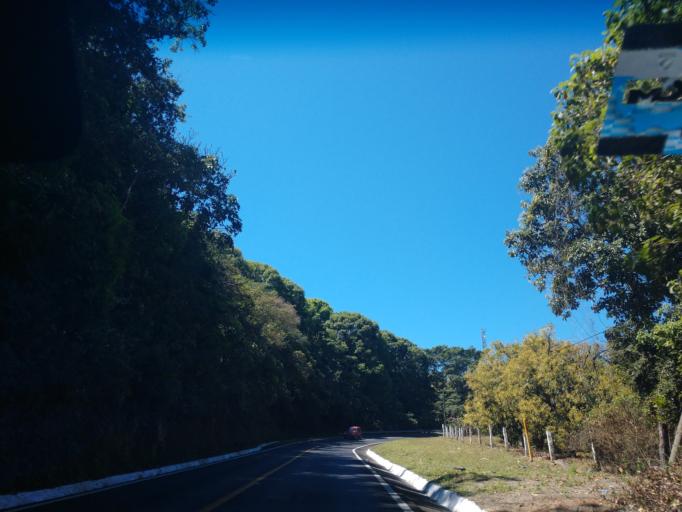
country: MX
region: Nayarit
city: Xalisco
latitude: 21.3704
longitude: -104.9017
